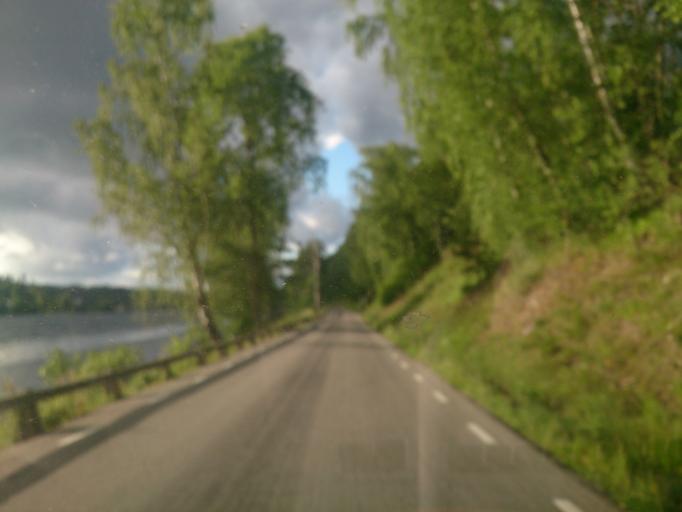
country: SE
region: OEstergoetland
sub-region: Norrkopings Kommun
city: Jursla
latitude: 58.7089
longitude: 16.1538
